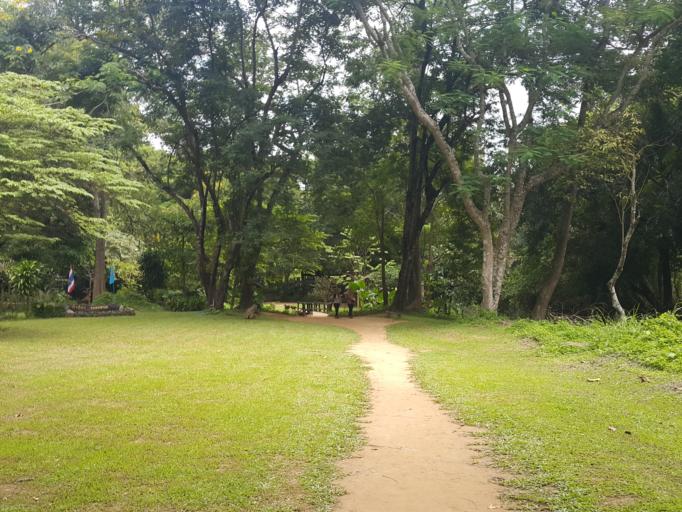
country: TH
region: Mae Hong Son
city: Mae Hong Son
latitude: 19.4267
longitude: 97.9895
